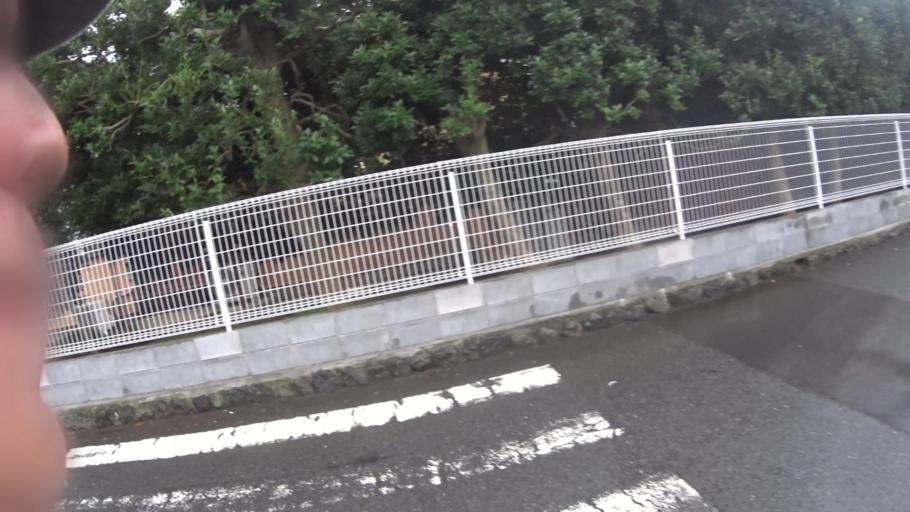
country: JP
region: Kanagawa
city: Hadano
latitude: 35.3666
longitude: 139.2168
